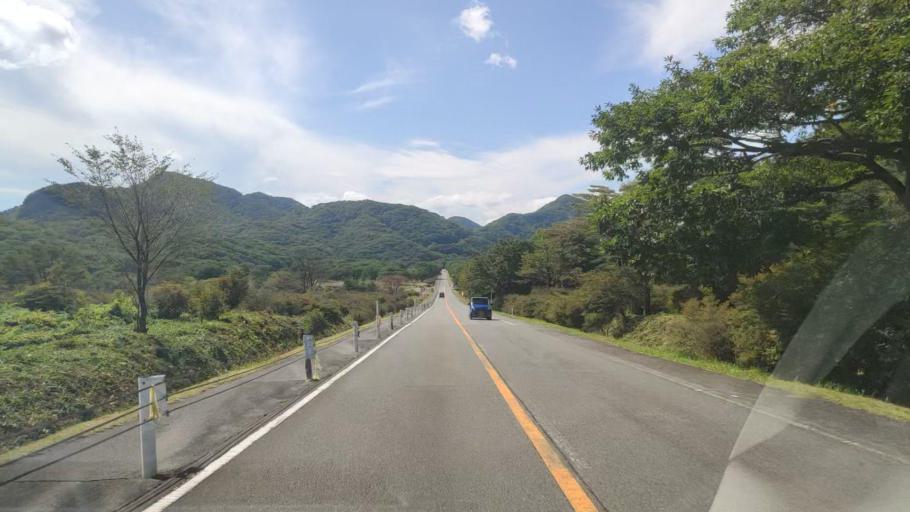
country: JP
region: Gunma
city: Shibukawa
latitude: 36.4770
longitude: 138.8905
